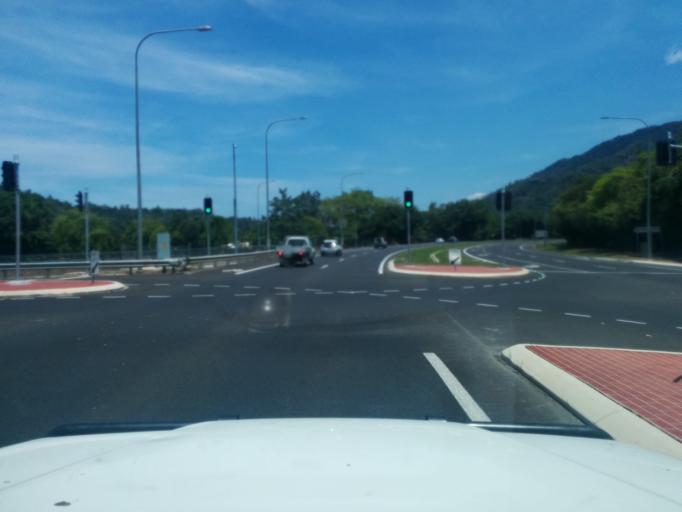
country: AU
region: Queensland
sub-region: Cairns
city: Redlynch
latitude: -16.8962
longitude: 145.7091
